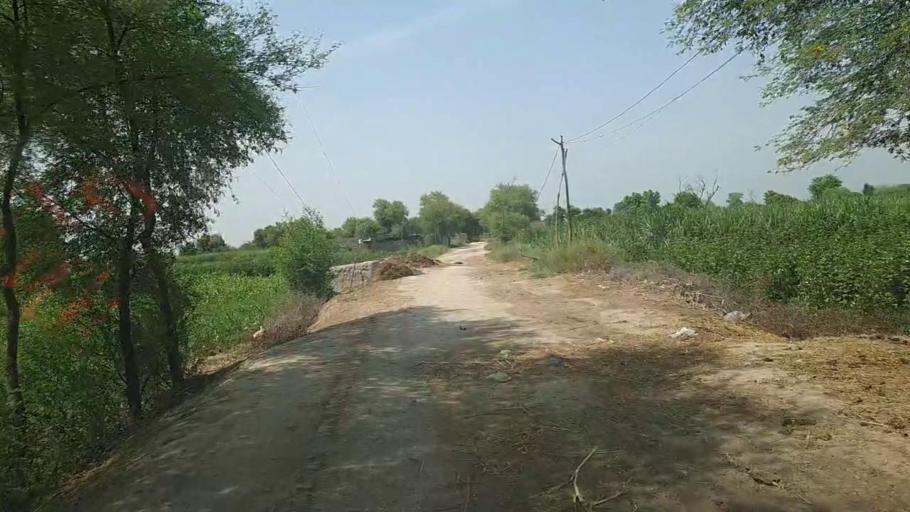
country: PK
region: Sindh
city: Ubauro
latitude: 28.1686
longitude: 69.8163
